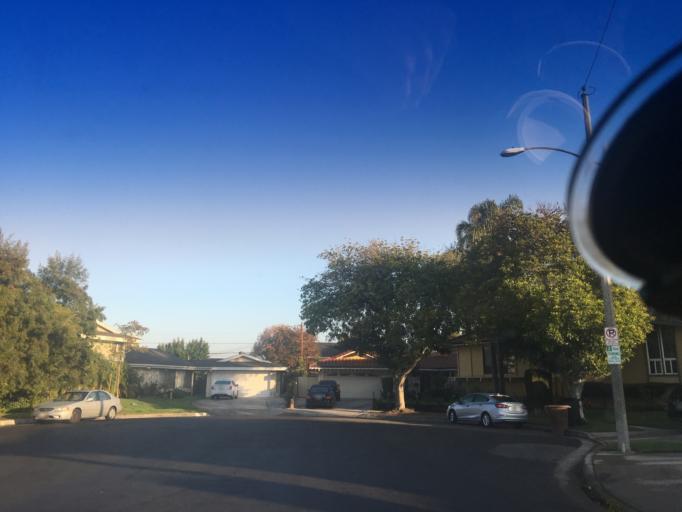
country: US
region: California
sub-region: Orange County
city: Anaheim
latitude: 33.8266
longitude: -117.8834
